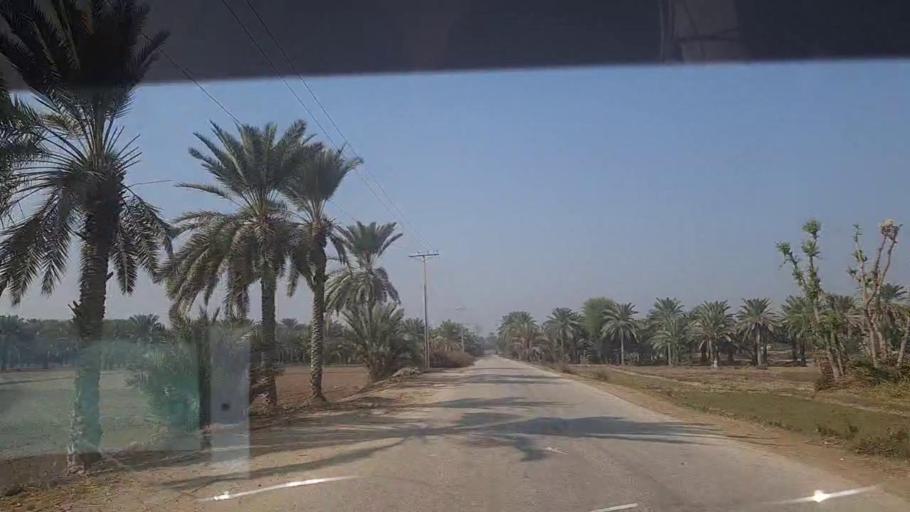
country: PK
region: Sindh
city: Kot Diji
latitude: 27.3758
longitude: 68.6949
